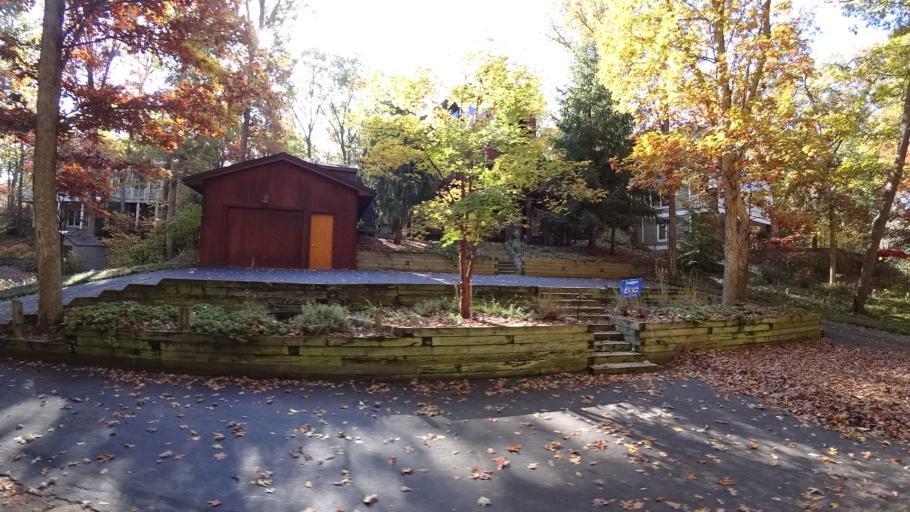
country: US
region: Indiana
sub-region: LaPorte County
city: Long Beach
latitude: 41.7534
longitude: -86.8350
